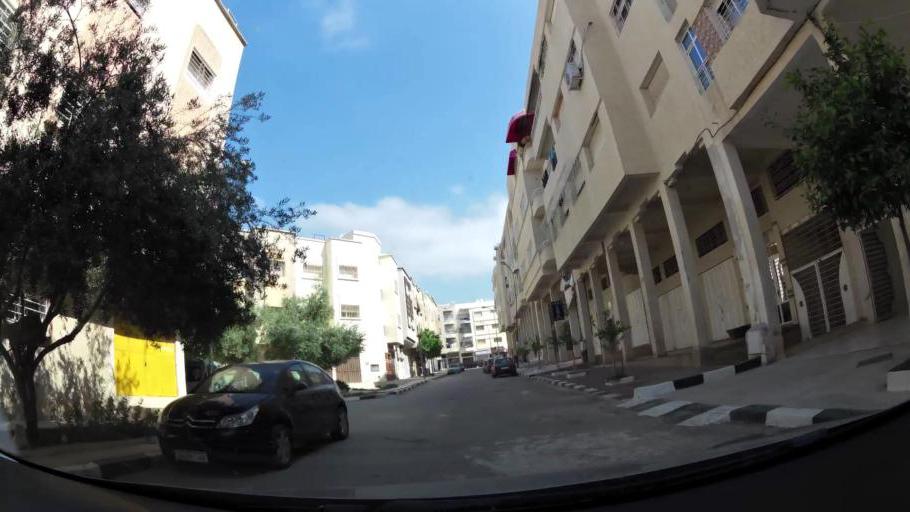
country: MA
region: Fes-Boulemane
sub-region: Fes
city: Fes
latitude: 34.0562
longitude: -5.0277
